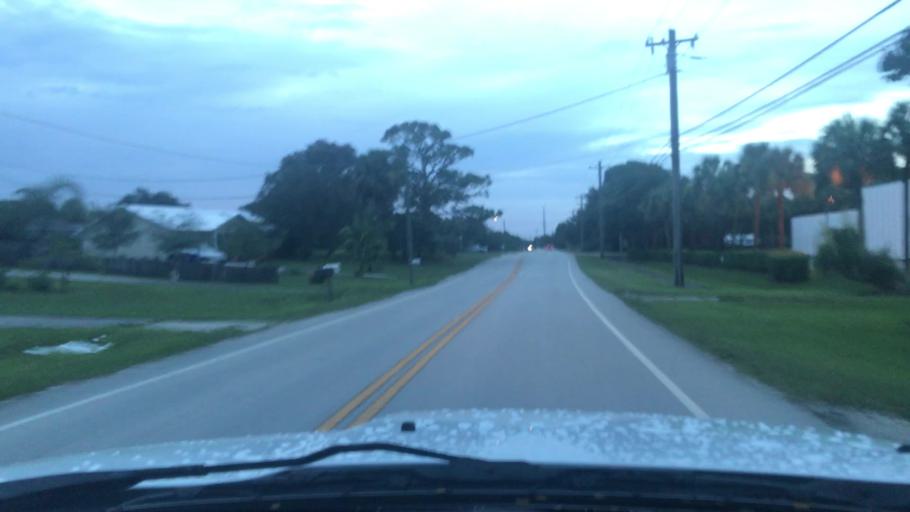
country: US
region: Florida
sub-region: Indian River County
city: Florida Ridge
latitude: 27.5985
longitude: -80.3847
